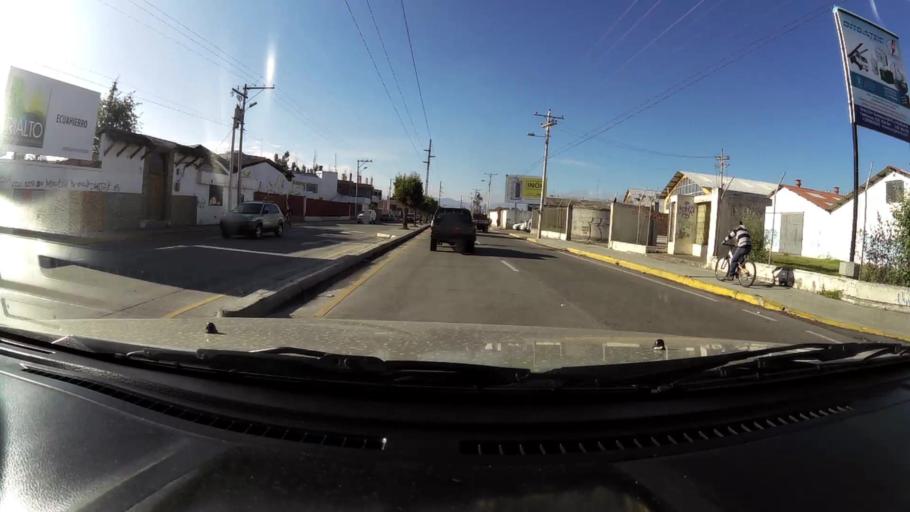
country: EC
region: Chimborazo
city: Riobamba
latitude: -1.6839
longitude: -78.6302
